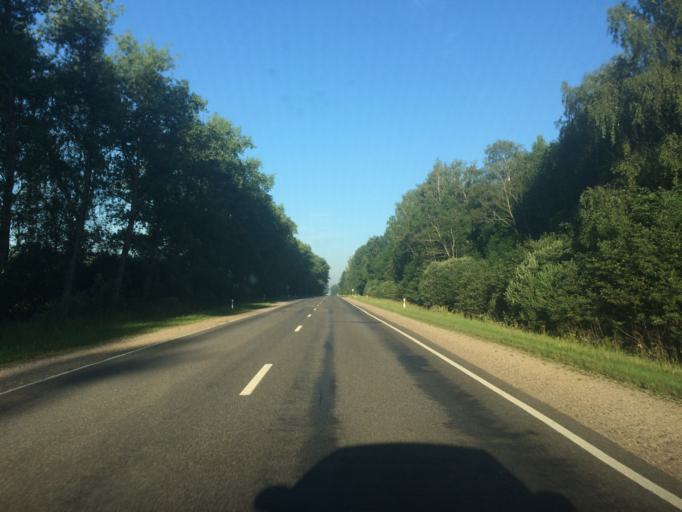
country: LT
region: Utenos apskritis
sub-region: Anyksciai
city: Anyksciai
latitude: 55.3590
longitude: 24.9772
